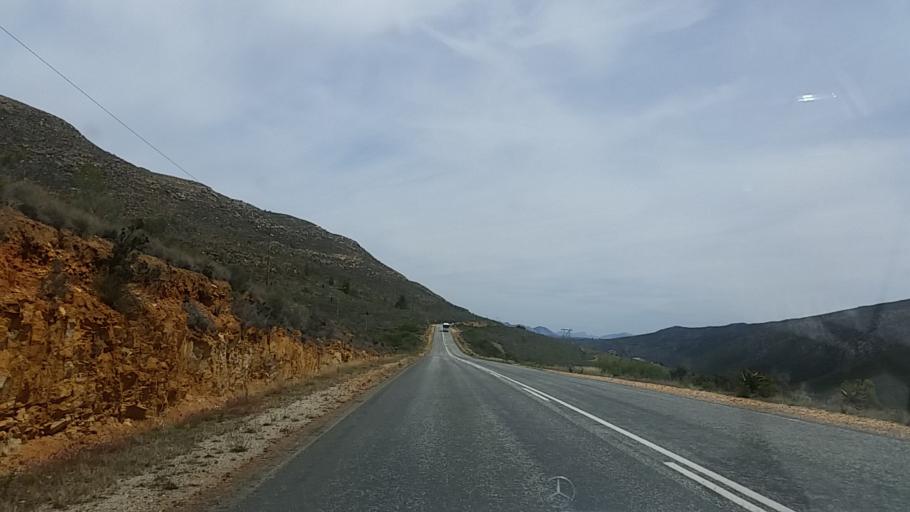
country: ZA
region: Western Cape
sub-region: Eden District Municipality
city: Knysna
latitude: -33.7448
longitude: 22.9905
